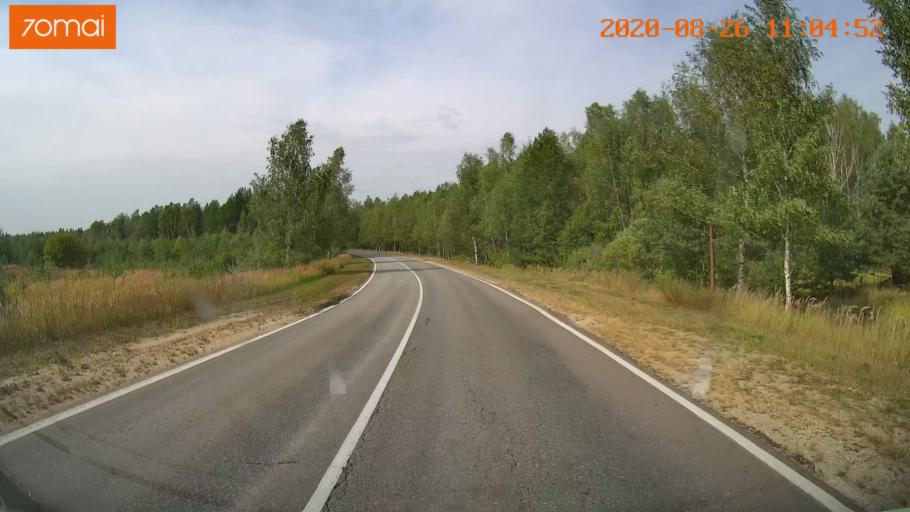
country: RU
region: Rjazan
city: Izhevskoye
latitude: 54.5296
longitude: 41.1864
